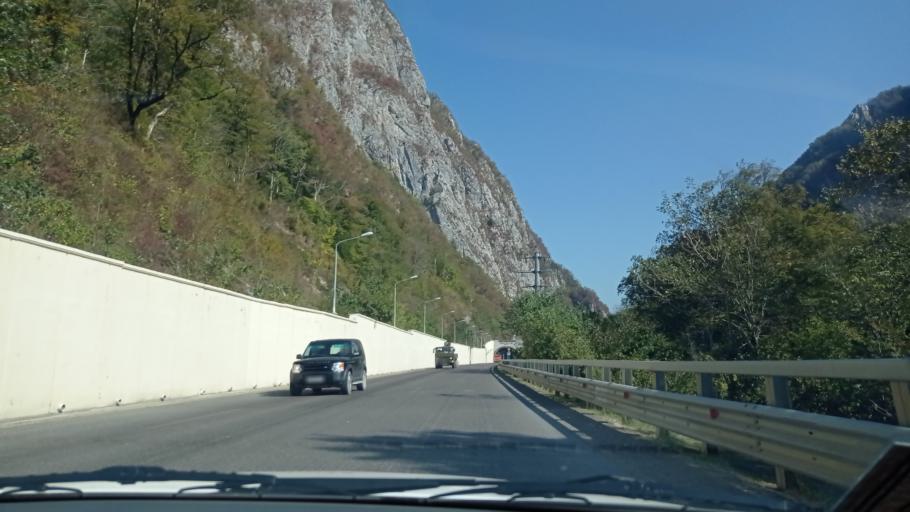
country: RU
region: Krasnodarskiy
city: Vysokoye
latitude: 43.5962
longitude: 40.0204
